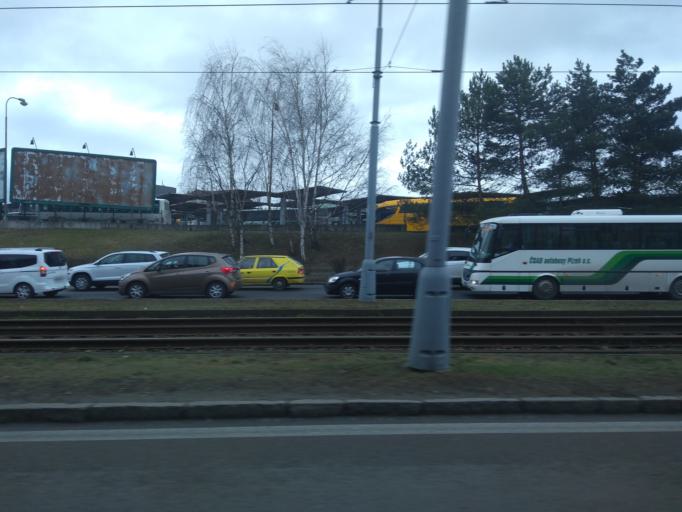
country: CZ
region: Plzensky
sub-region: Okres Plzen-Mesto
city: Pilsen
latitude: 49.7475
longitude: 13.3625
